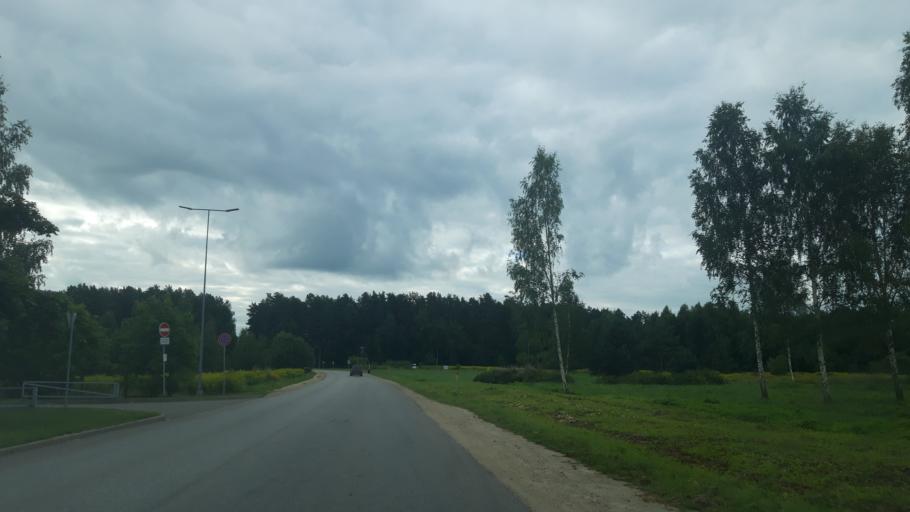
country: LV
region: Koceni
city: Koceni
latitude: 57.5231
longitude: 25.3809
